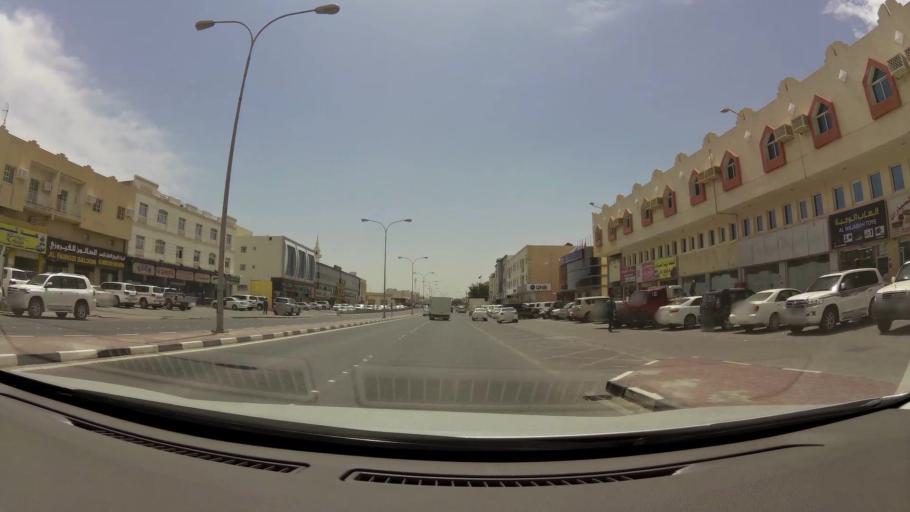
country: QA
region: Baladiyat ar Rayyan
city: Ar Rayyan
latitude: 25.2968
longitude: 51.4202
